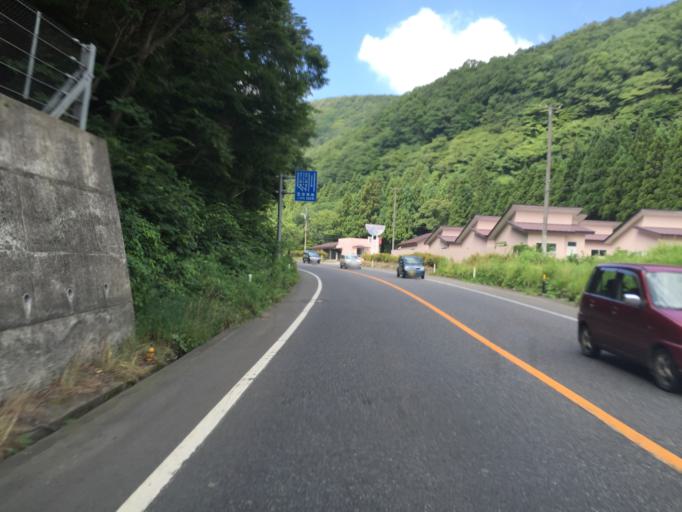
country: JP
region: Fukushima
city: Inawashiro
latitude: 37.4941
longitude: 140.2089
